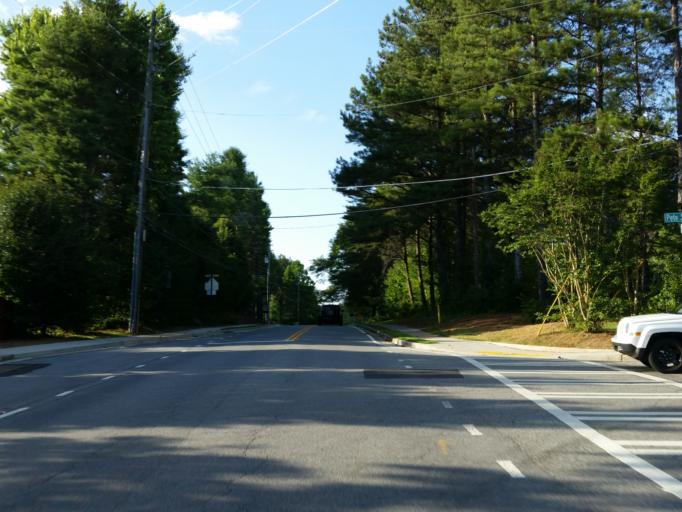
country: US
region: Georgia
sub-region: Cherokee County
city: Woodstock
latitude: 34.0462
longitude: -84.4763
